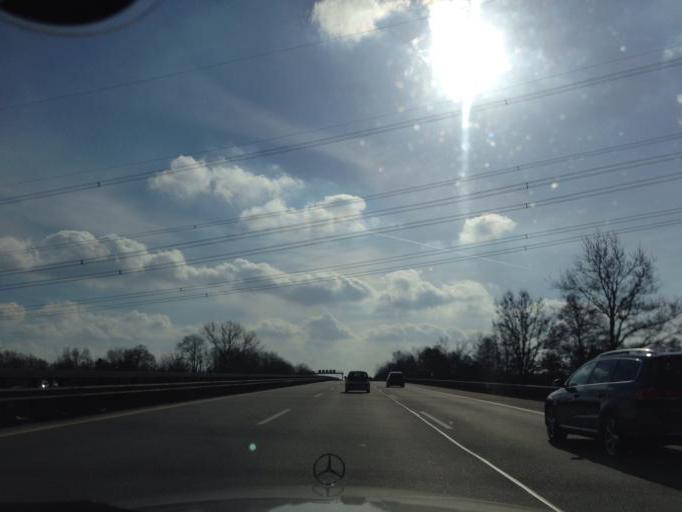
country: DE
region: Hamburg
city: Harburg
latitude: 53.4494
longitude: 10.0291
